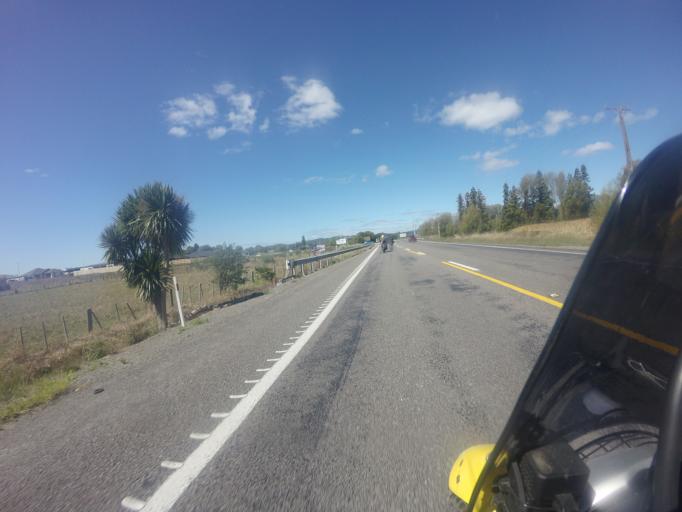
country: NZ
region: Bay of Plenty
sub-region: Whakatane District
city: Whakatane
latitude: -37.9507
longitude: 176.9482
